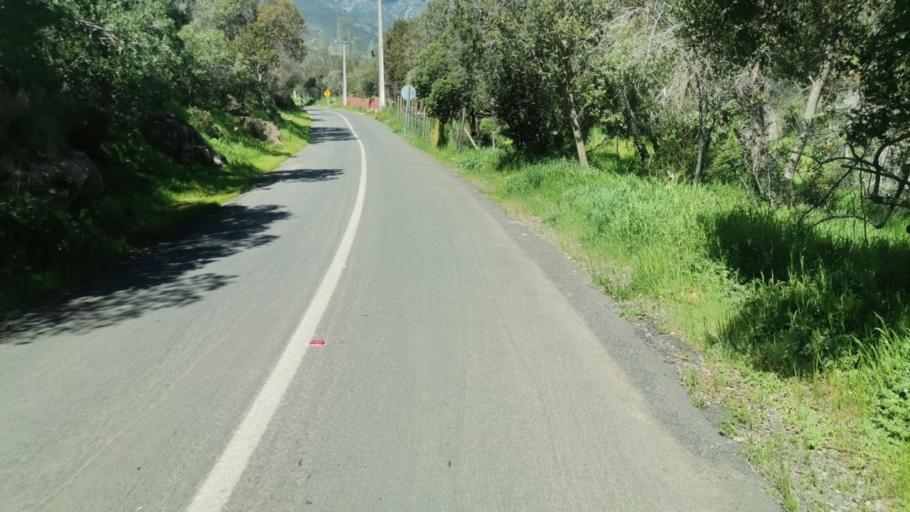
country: CL
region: Valparaiso
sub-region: Provincia de Marga Marga
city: Limache
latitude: -33.1829
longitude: -71.1102
